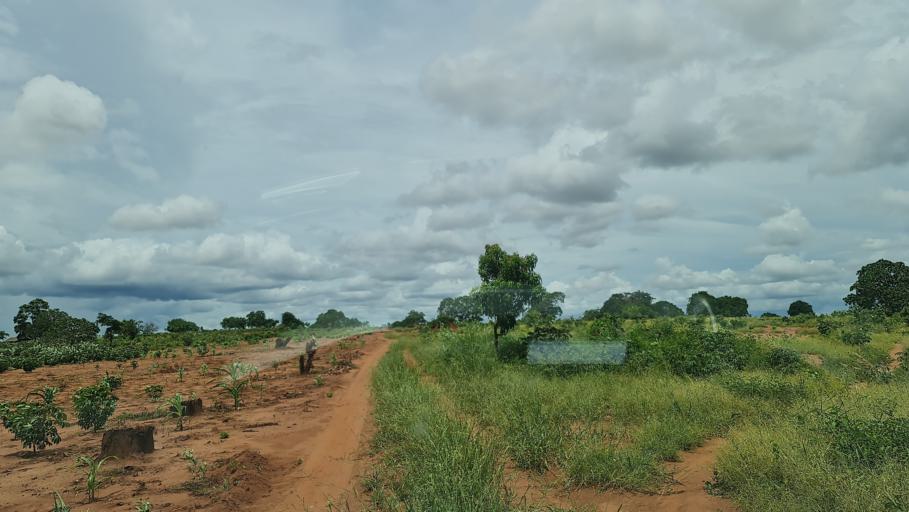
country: MZ
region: Nampula
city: Nacala
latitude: -14.7866
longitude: 39.9782
